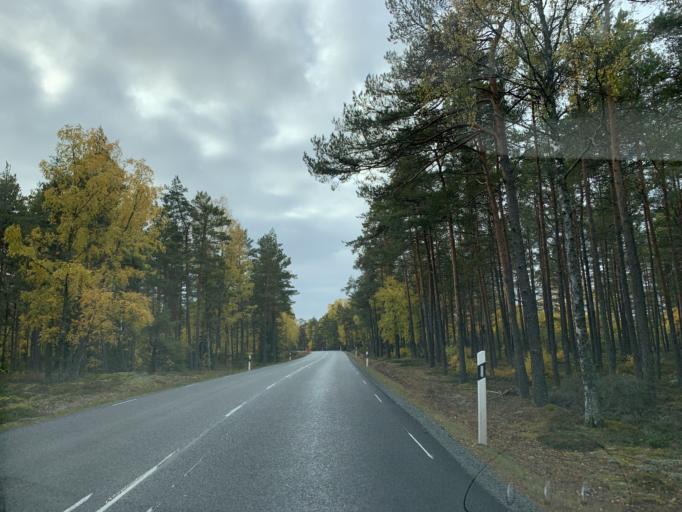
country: SE
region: Stockholm
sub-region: Botkyrka Kommun
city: Varsta
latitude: 59.0778
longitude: 17.7868
